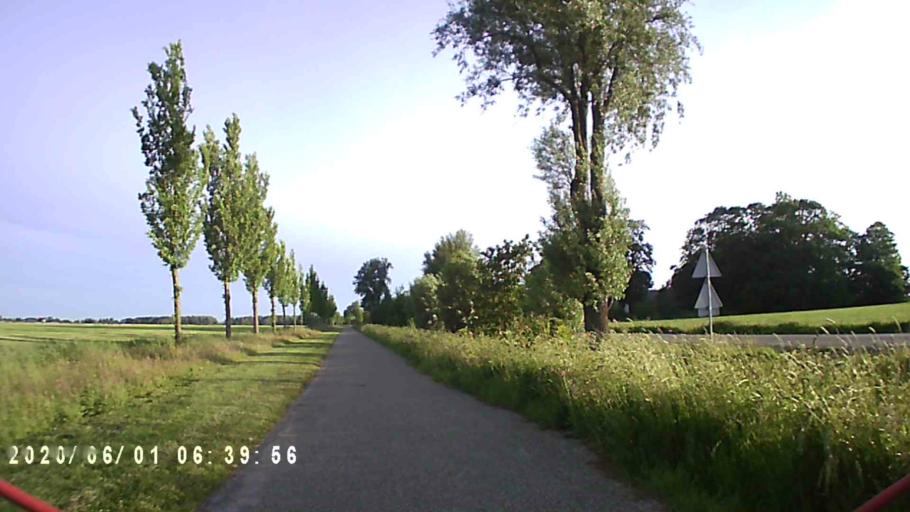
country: NL
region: Friesland
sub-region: Gemeente Kollumerland en Nieuwkruisland
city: Kollum
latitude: 53.2913
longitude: 6.1585
